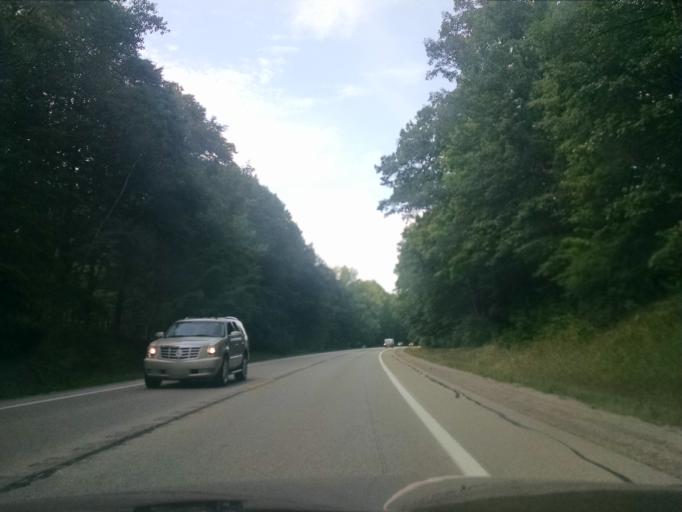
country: US
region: Michigan
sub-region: Clare County
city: Clare
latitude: 43.8732
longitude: -84.9428
